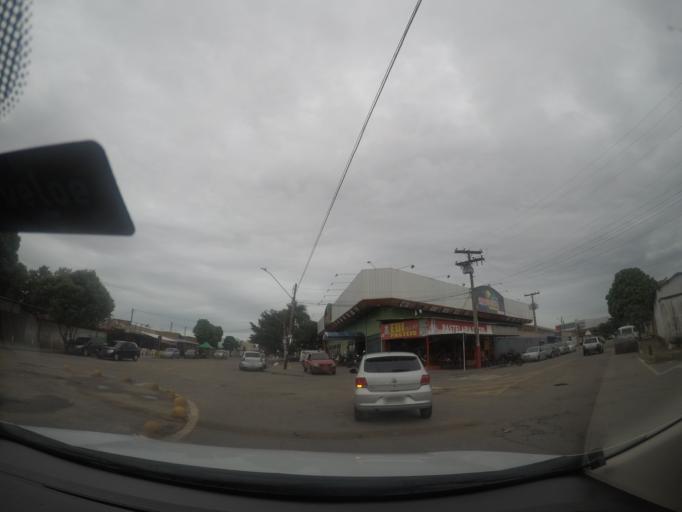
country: BR
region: Goias
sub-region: Goiania
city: Goiania
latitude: -16.6849
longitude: -49.3323
